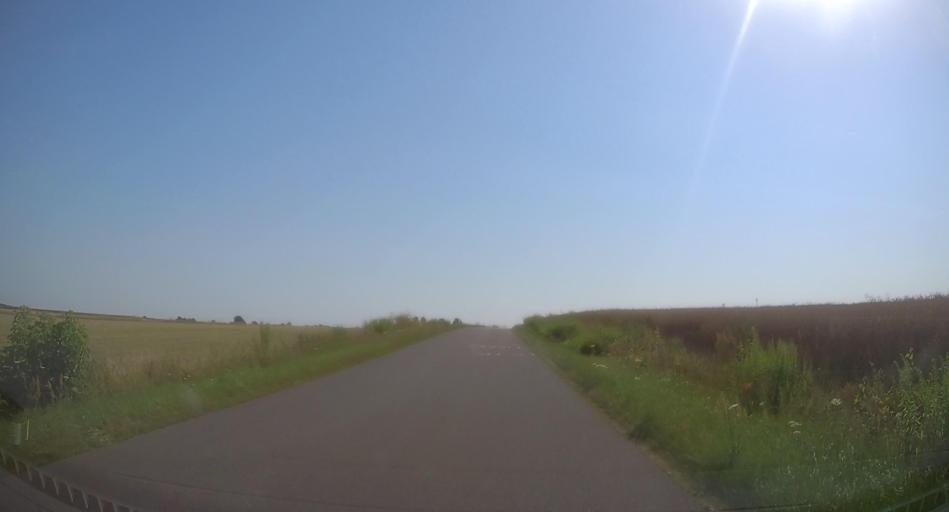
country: PL
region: Lodz Voivodeship
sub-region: Powiat skierniewicki
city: Kaweczyn Nowy
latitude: 51.8852
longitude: 20.2230
